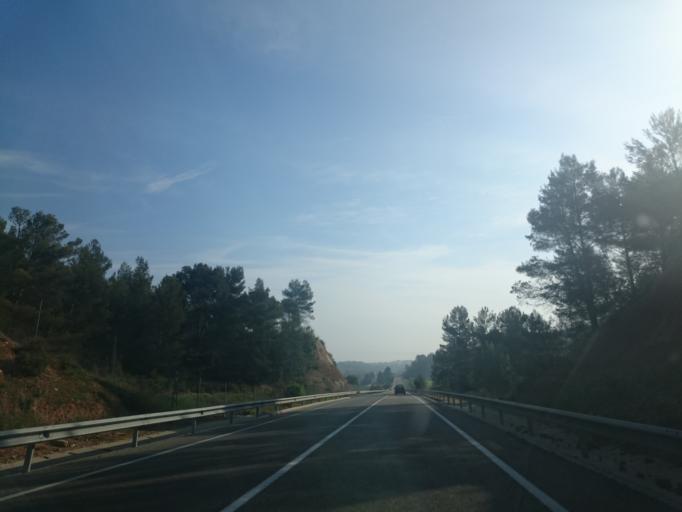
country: ES
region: Catalonia
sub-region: Provincia de Barcelona
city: Sant Salvador de Guardiola
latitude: 41.6642
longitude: 1.7401
